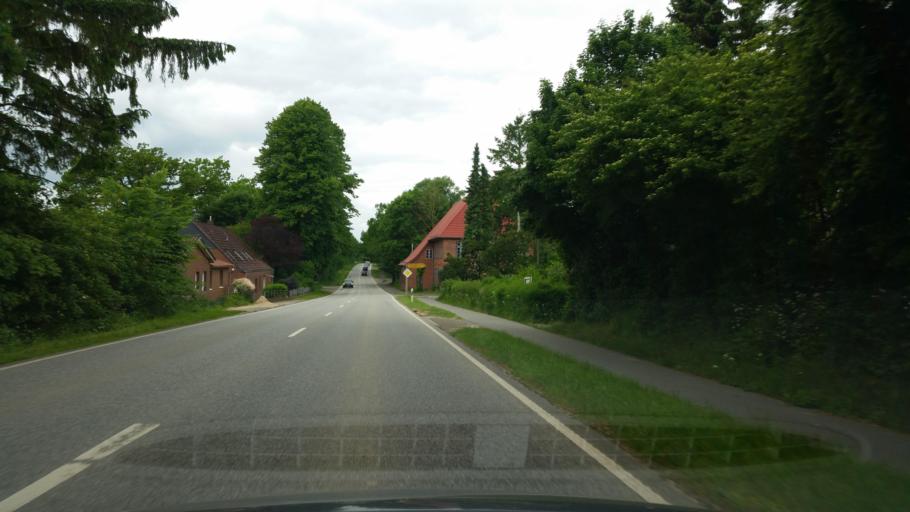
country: DE
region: Schleswig-Holstein
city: Glasau
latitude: 53.9991
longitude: 10.5053
